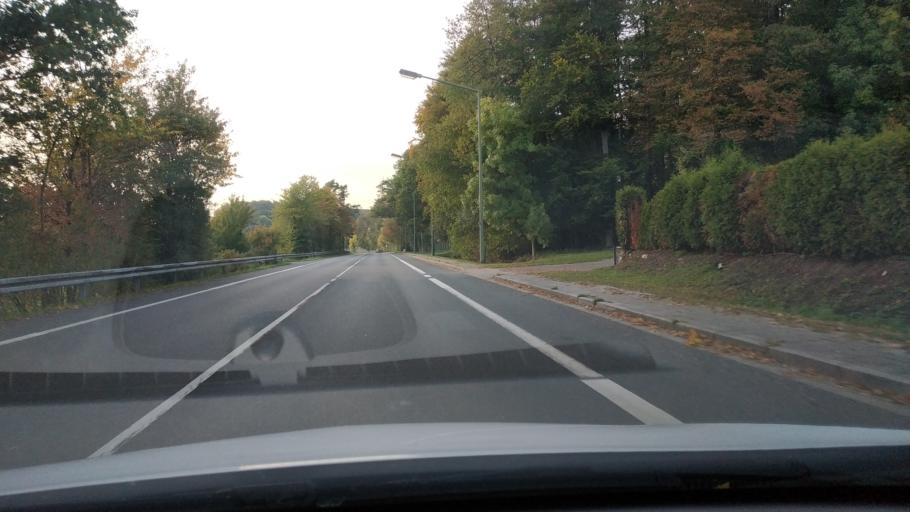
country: DE
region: Lower Saxony
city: Bissendorf
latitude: 52.2471
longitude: 8.1221
